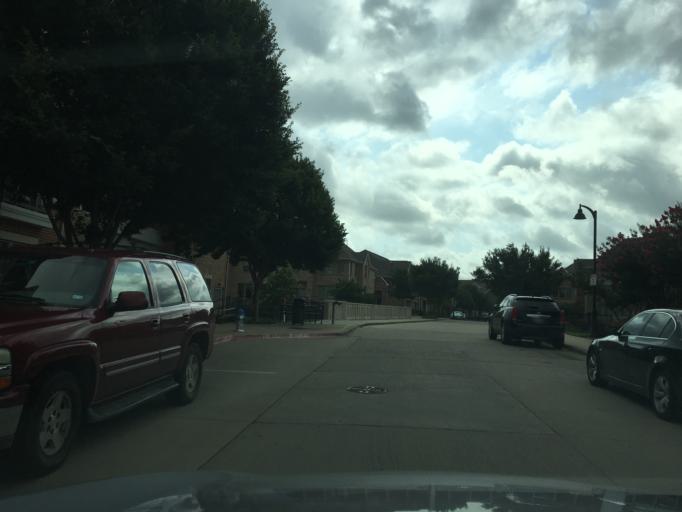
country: US
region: Texas
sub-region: Dallas County
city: Richardson
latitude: 32.9428
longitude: -96.7354
